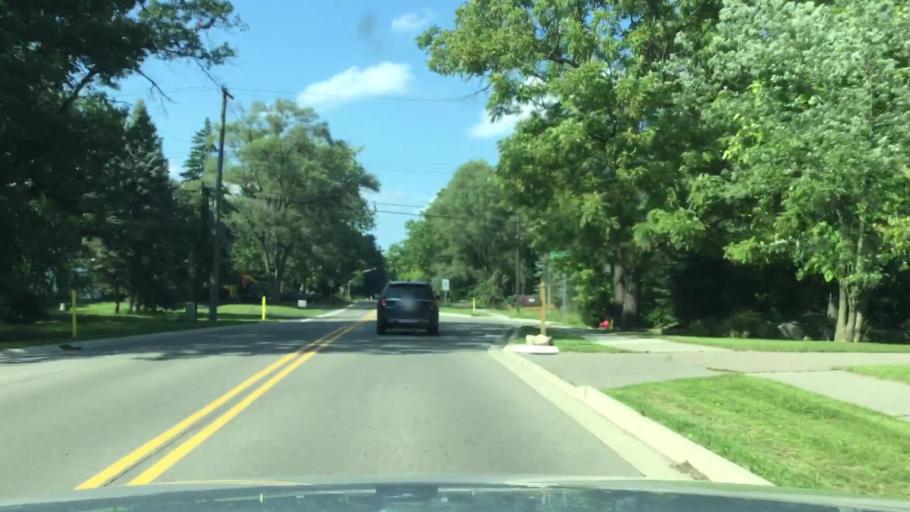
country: US
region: Michigan
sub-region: Oakland County
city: West Bloomfield Township
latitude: 42.5798
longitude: -83.4117
